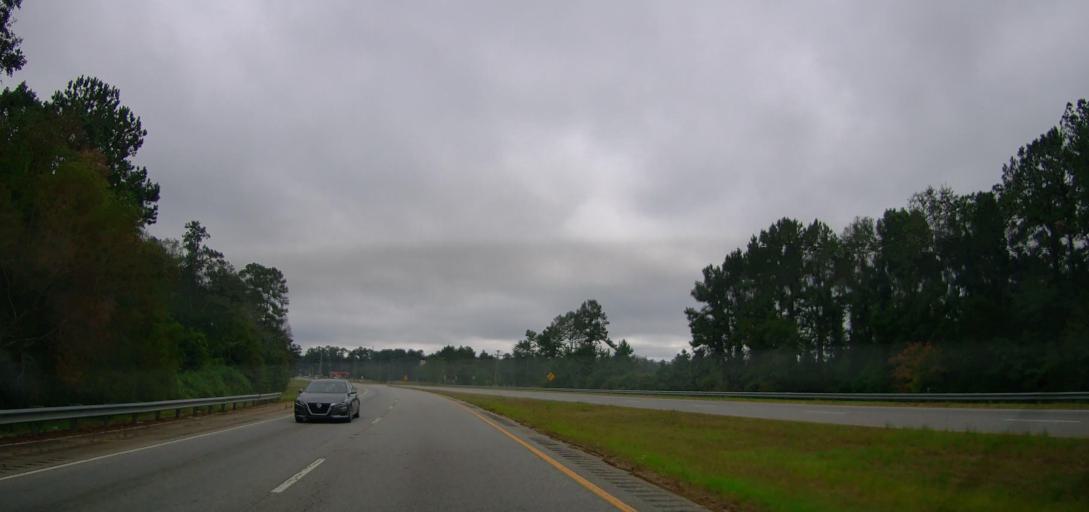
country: US
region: Georgia
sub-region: Thomas County
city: Thomasville
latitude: 30.8208
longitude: -84.0053
